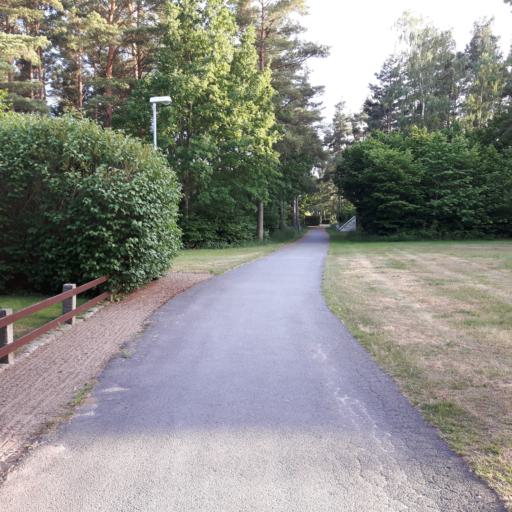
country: SE
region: Skane
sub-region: Hassleholms Kommun
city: Vinslov
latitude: 56.0965
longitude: 13.9059
